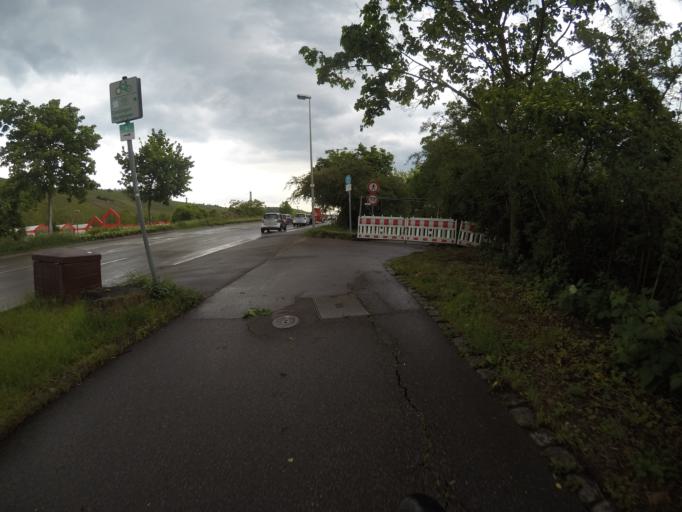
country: DE
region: Baden-Wuerttemberg
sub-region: Regierungsbezirk Stuttgart
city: Fellbach
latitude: 48.7744
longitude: 9.2574
